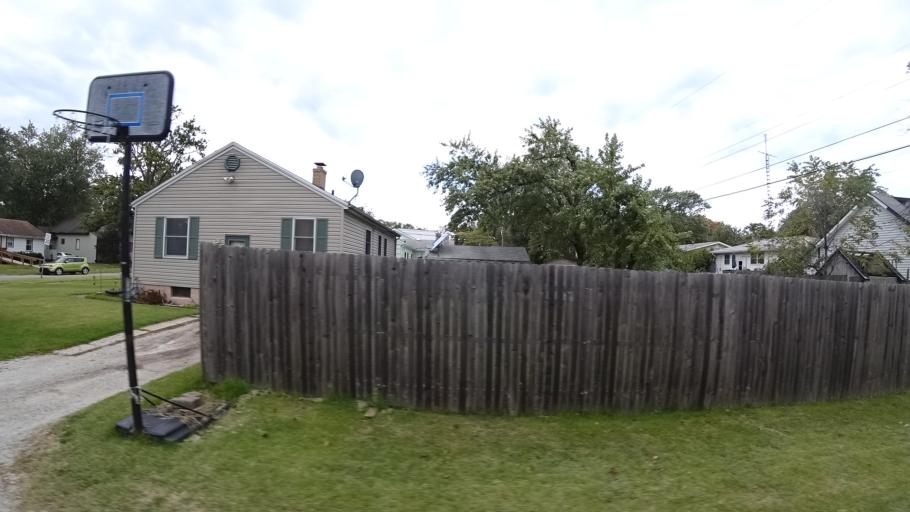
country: US
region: Indiana
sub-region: LaPorte County
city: Michigan City
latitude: 41.6989
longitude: -86.8876
